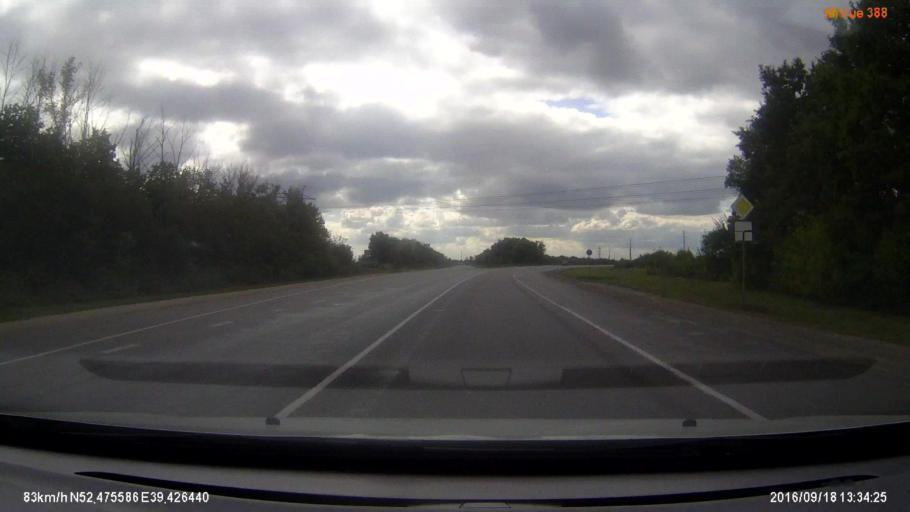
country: RU
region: Lipetsk
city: Borinskoye
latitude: 52.4877
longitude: 39.4417
